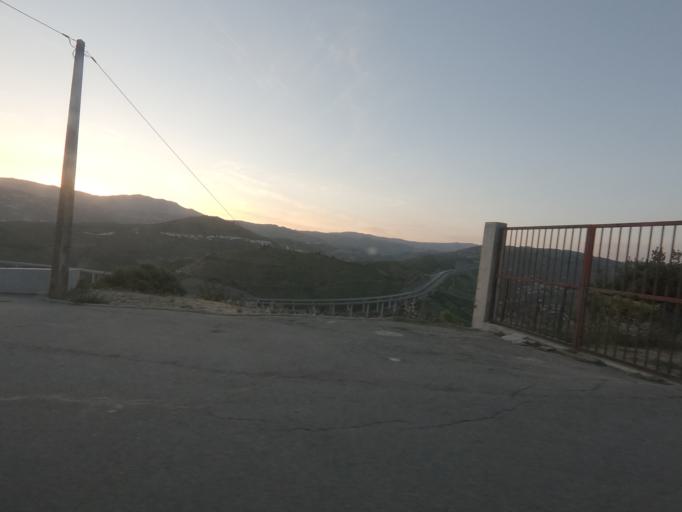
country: PT
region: Vila Real
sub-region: Peso da Regua
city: Peso da Regua
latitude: 41.1678
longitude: -7.7485
